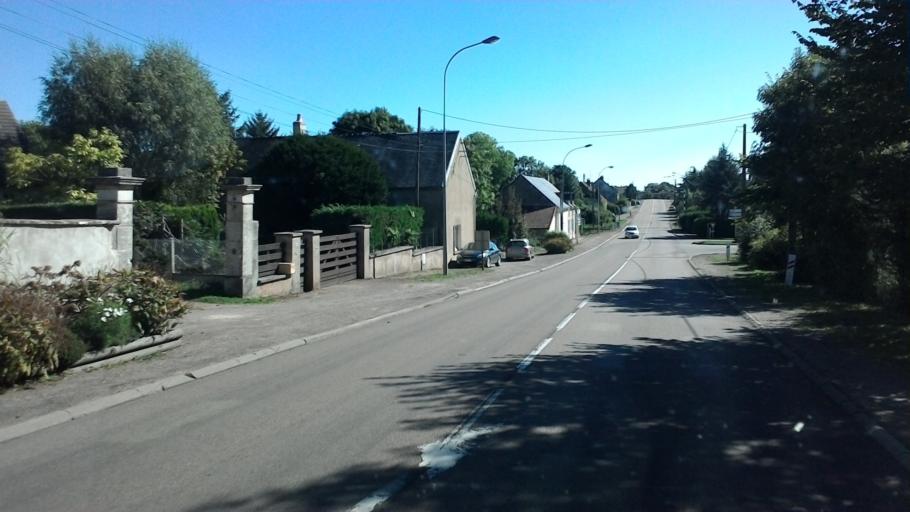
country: FR
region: Bourgogne
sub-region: Departement de la Cote-d'Or
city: Saulieu
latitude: 47.2778
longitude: 4.2373
